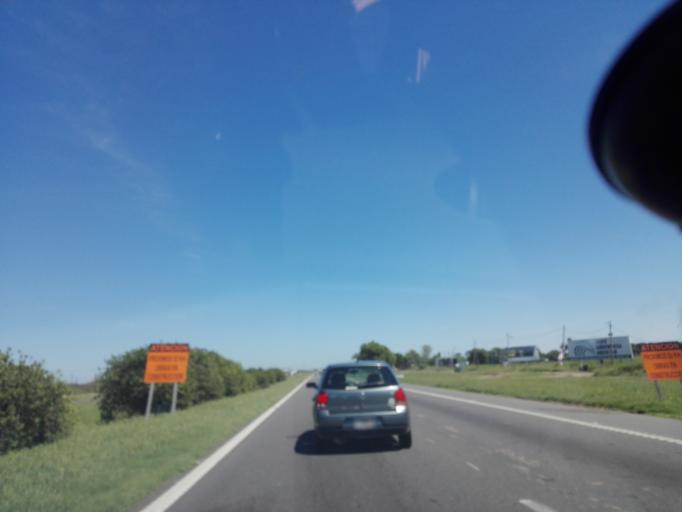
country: AR
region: Buenos Aires
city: San Nicolas de los Arroyos
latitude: -33.3829
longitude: -60.2295
